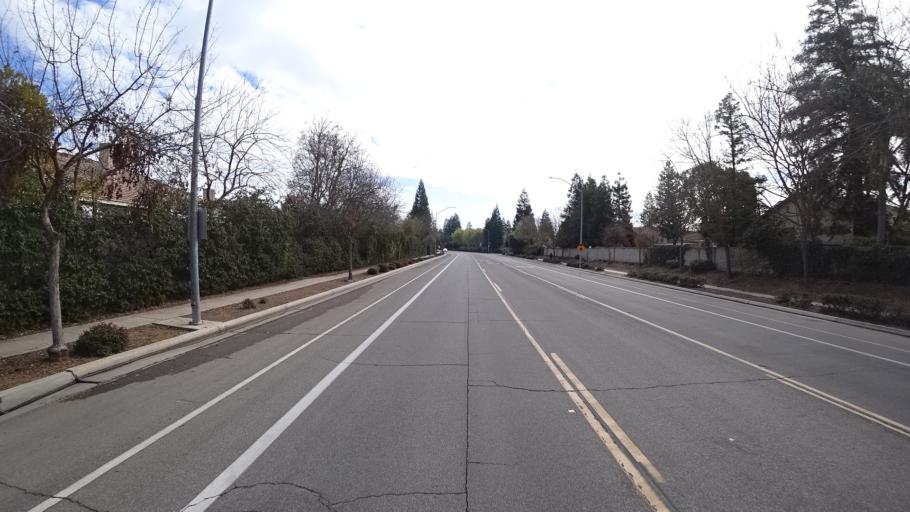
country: US
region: California
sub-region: Fresno County
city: Biola
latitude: 36.8479
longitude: -119.8910
